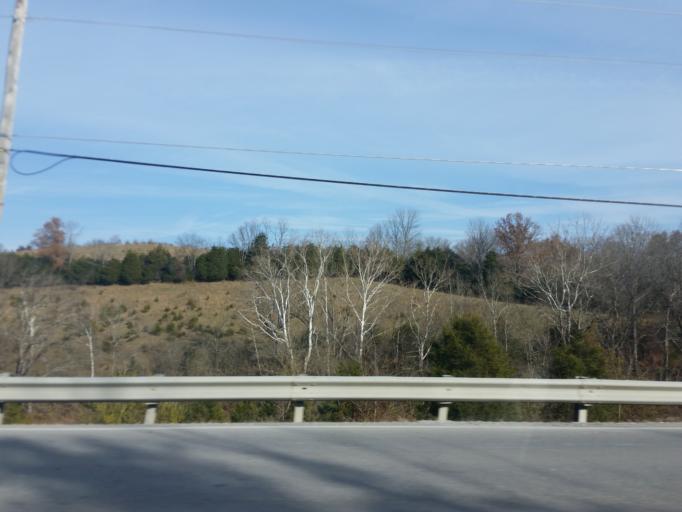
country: US
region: Kentucky
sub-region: Campbell County
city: Claryville
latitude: 38.8006
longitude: -84.3569
